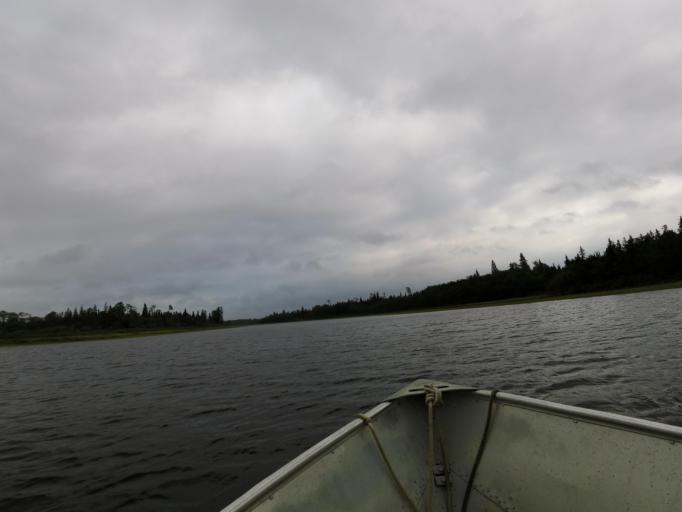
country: CA
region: Ontario
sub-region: Rainy River District
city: Atikokan
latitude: 49.5914
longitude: -91.3622
